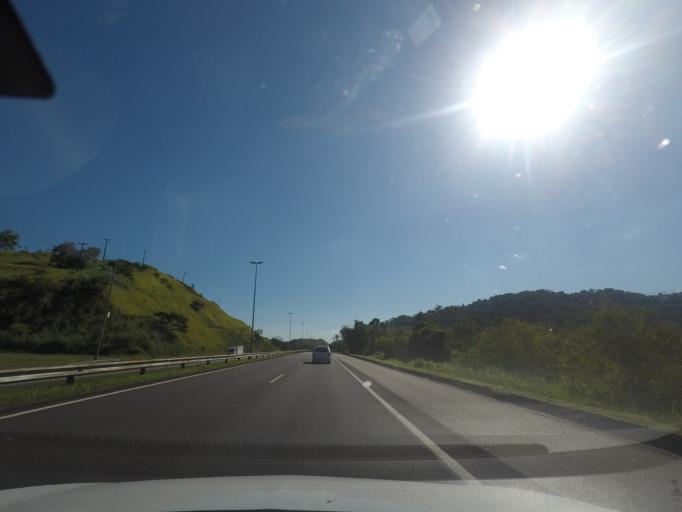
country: BR
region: Rio de Janeiro
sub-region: Guapimirim
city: Guapimirim
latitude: -22.6300
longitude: -43.0507
